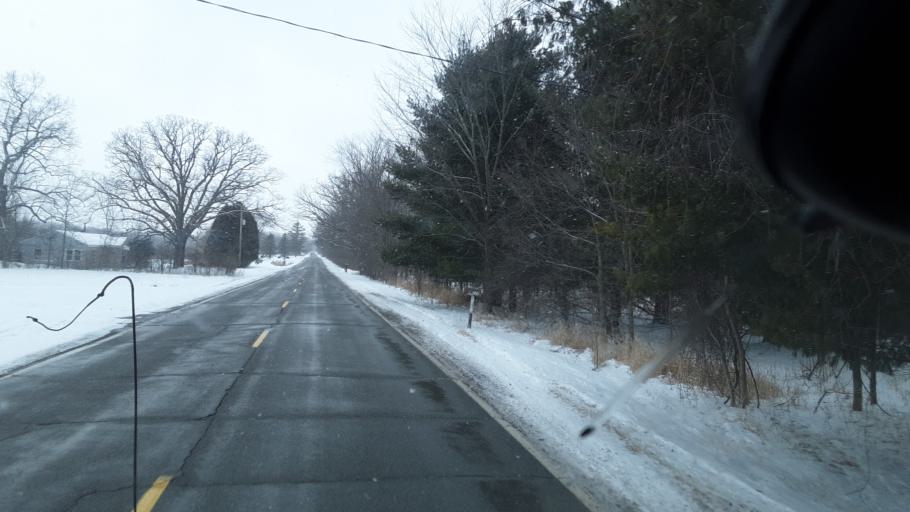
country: US
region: Michigan
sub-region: Ingham County
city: Leslie
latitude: 42.4717
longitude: -84.3403
